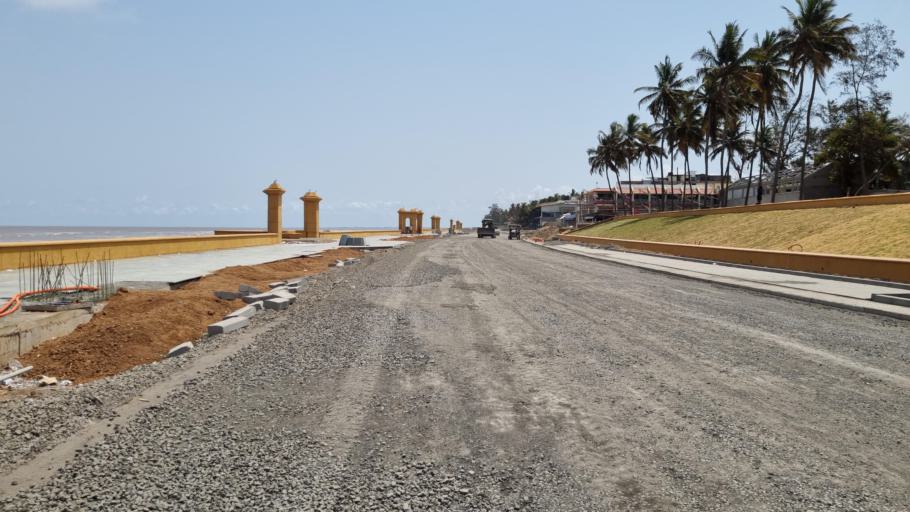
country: IN
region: Daman and Diu
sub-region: Daman District
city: Daman
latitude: 20.4466
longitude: 72.8330
